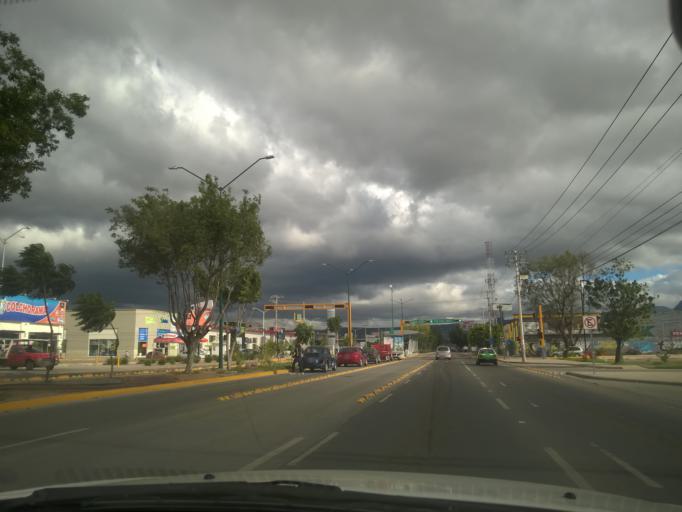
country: MX
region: Guanajuato
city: Leon
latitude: 21.1239
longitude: -101.6486
